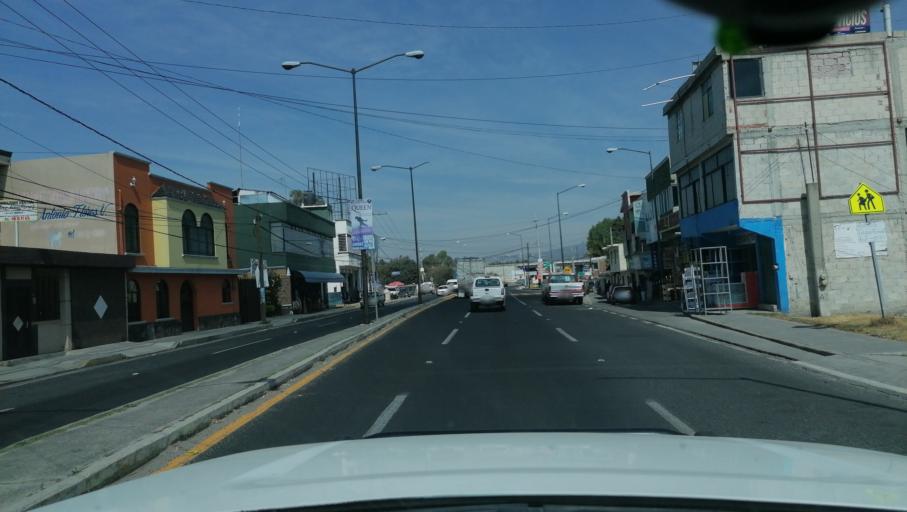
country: MX
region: Tlaxcala
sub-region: Tepeyanco
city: Santiago Tlacochcalco
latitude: 19.2817
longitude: -98.2380
